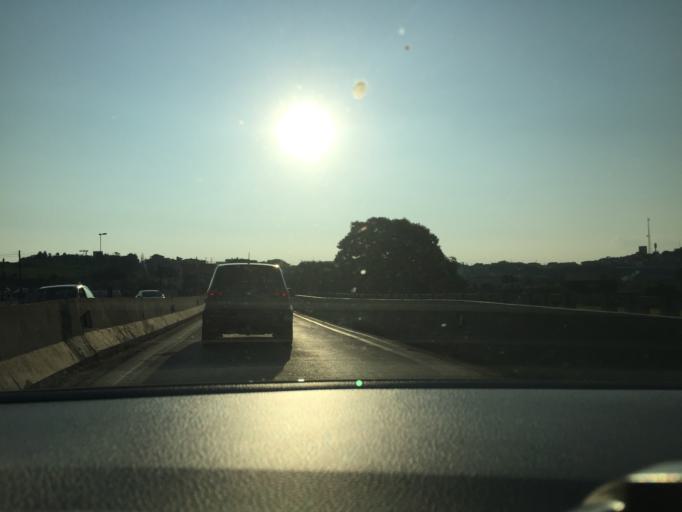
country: BR
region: Sao Paulo
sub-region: Louveira
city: Louveira
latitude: -23.0963
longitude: -46.9688
